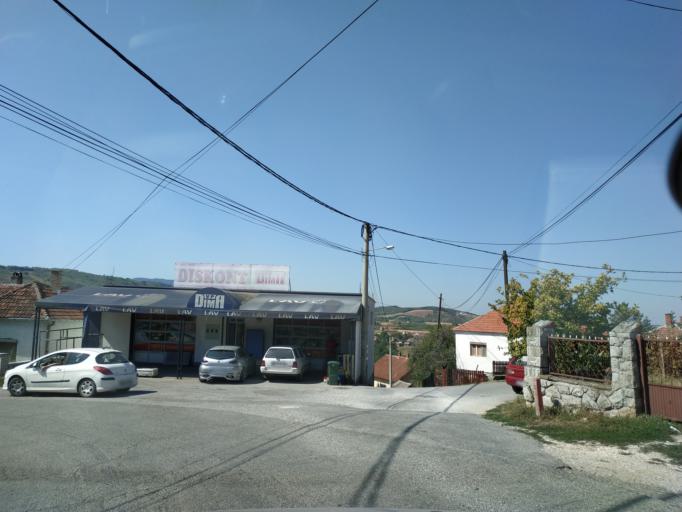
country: RS
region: Central Serbia
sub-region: Sumadijski Okrug
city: Topola
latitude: 44.2562
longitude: 20.6747
